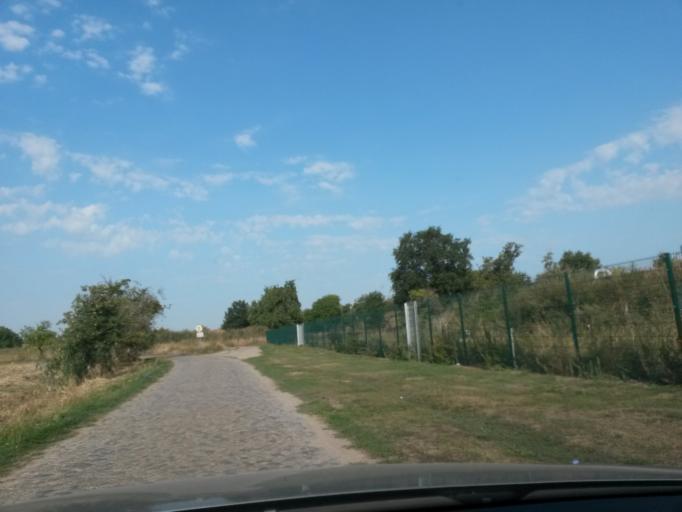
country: DE
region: Saxony-Anhalt
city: Tangermunde
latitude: 52.5412
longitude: 12.0094
